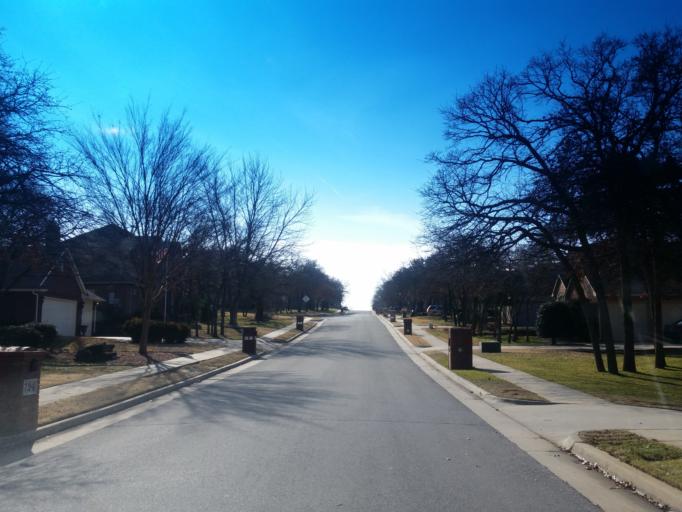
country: US
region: Oklahoma
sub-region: Oklahoma County
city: Edmond
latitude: 35.6465
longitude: -97.4333
